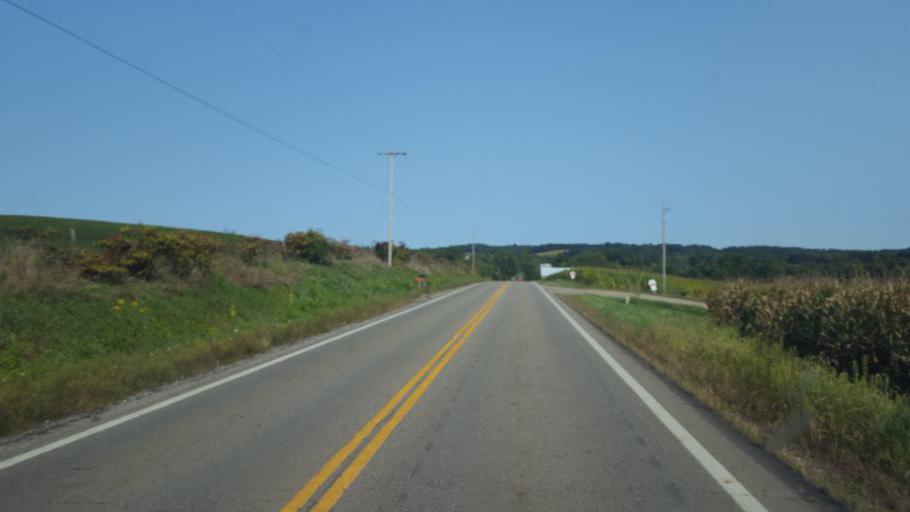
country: US
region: Ohio
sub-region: Ashland County
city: Loudonville
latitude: 40.6625
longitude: -82.1565
